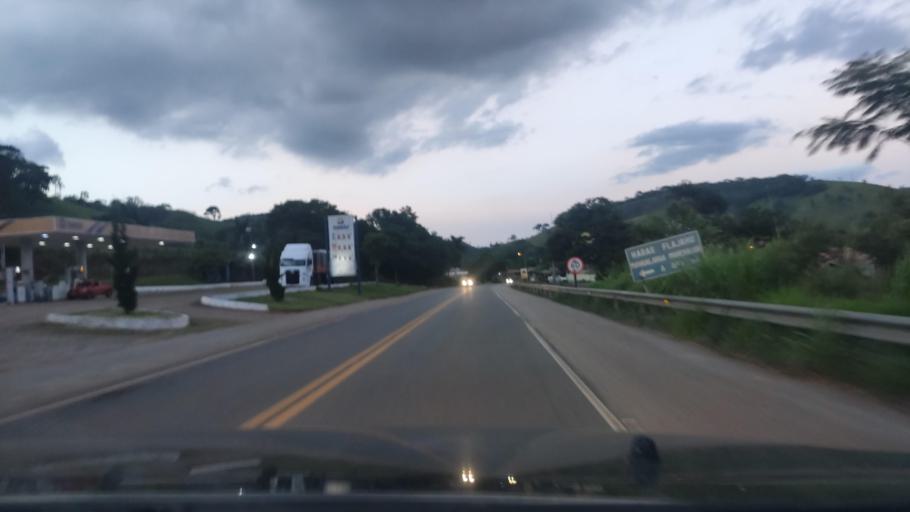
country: BR
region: Sao Paulo
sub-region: Campos Do Jordao
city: Campos do Jordao
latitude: -22.7884
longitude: -45.7435
